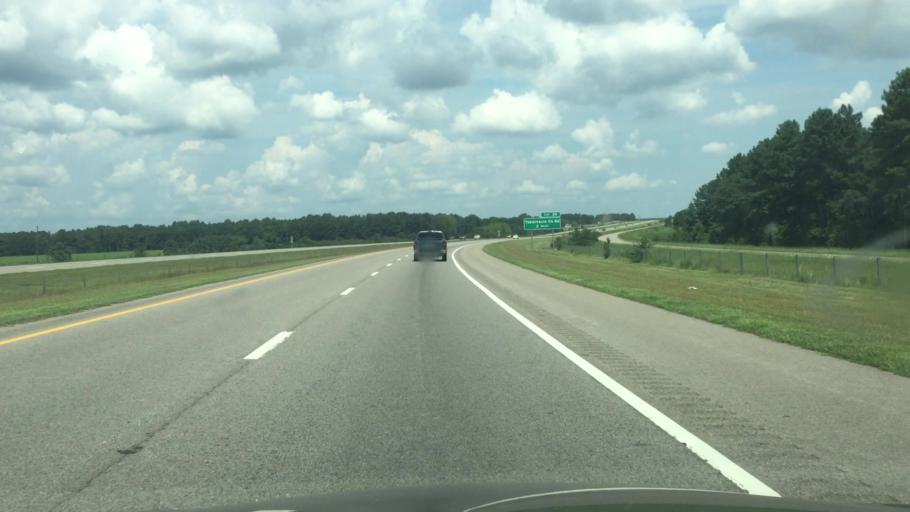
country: US
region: North Carolina
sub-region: Richmond County
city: Ellerbe
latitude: 35.1930
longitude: -79.7263
